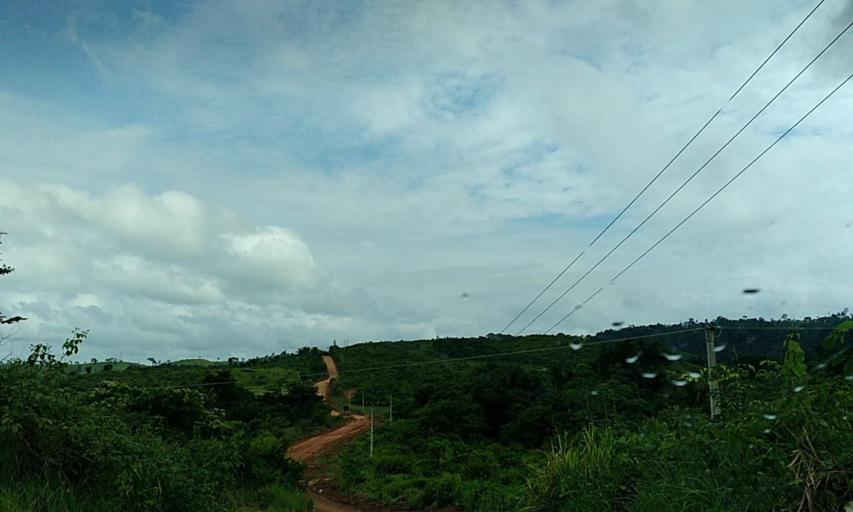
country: BR
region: Para
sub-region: Altamira
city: Altamira
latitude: -3.0888
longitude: -51.6344
